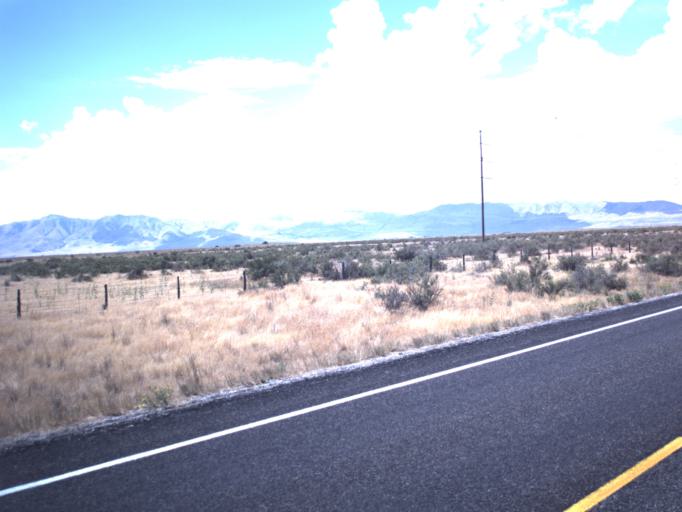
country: US
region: Utah
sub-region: Box Elder County
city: Tremonton
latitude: 41.5963
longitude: -112.2904
